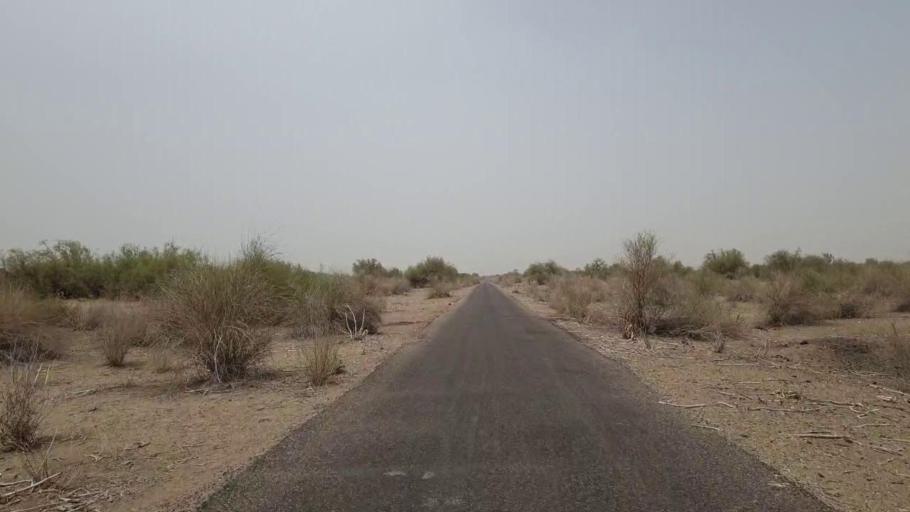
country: PK
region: Sindh
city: Islamkot
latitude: 24.7615
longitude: 70.4762
